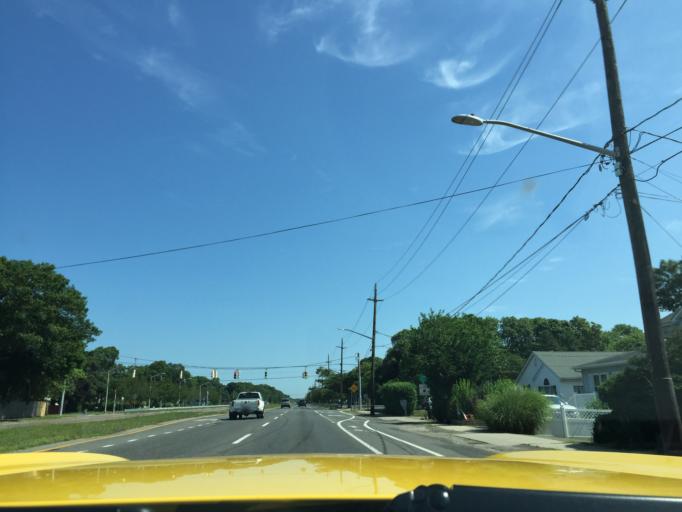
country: US
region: New York
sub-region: Suffolk County
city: Mastic Beach
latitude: 40.7631
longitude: -72.8706
